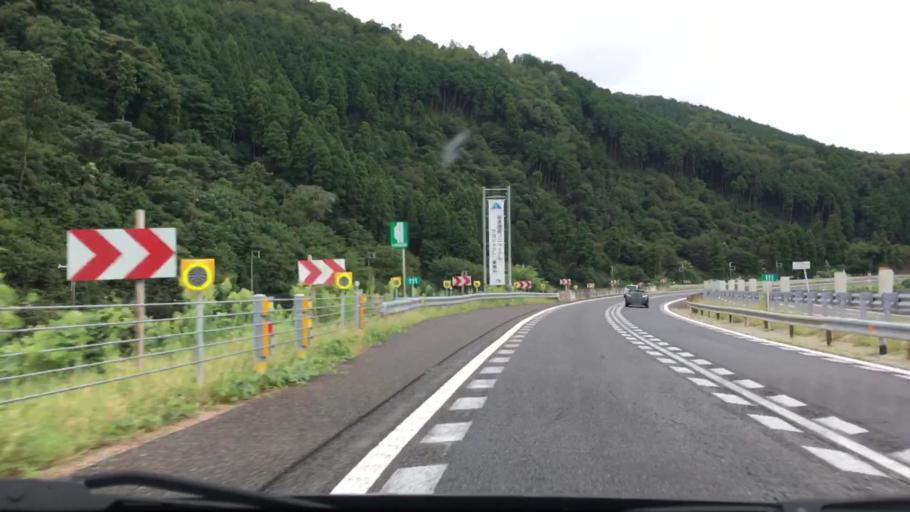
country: JP
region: Hyogo
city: Yamazakicho-nakabirose
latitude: 35.0433
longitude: 134.4495
